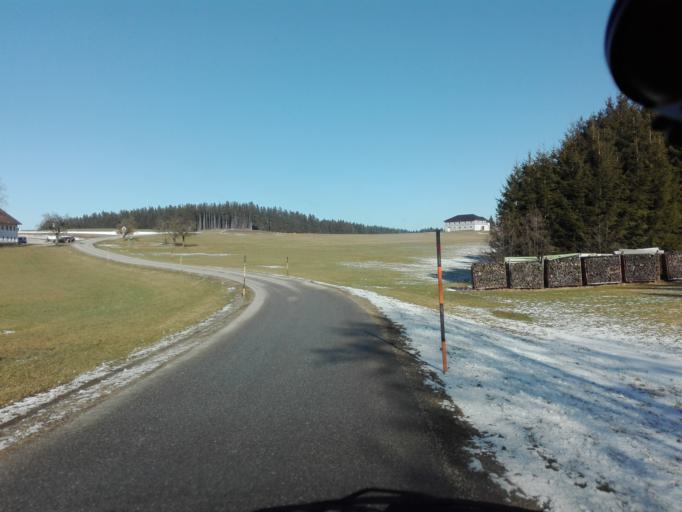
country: AT
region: Upper Austria
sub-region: Politischer Bezirk Urfahr-Umgebung
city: Sonnberg im Muehlkreis
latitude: 48.4580
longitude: 14.3033
